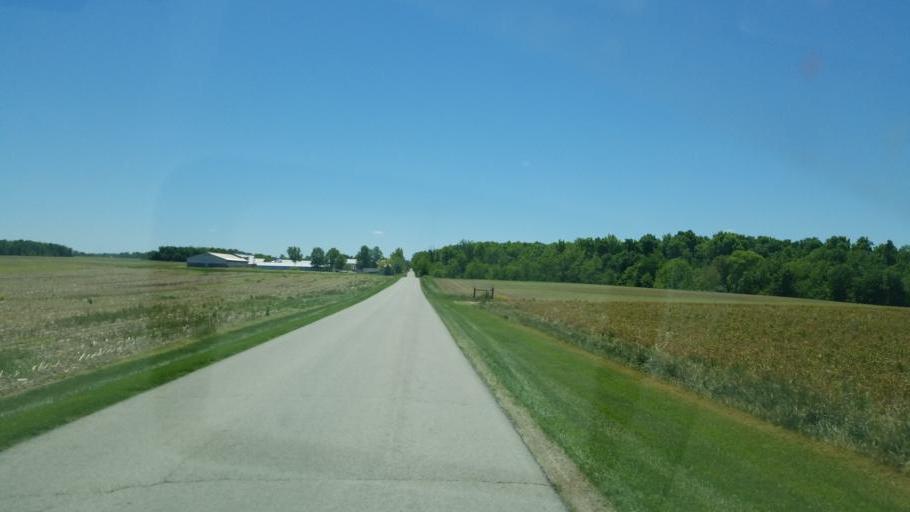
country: US
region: Ohio
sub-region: Mercer County
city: Fort Recovery
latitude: 40.3602
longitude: -84.8040
